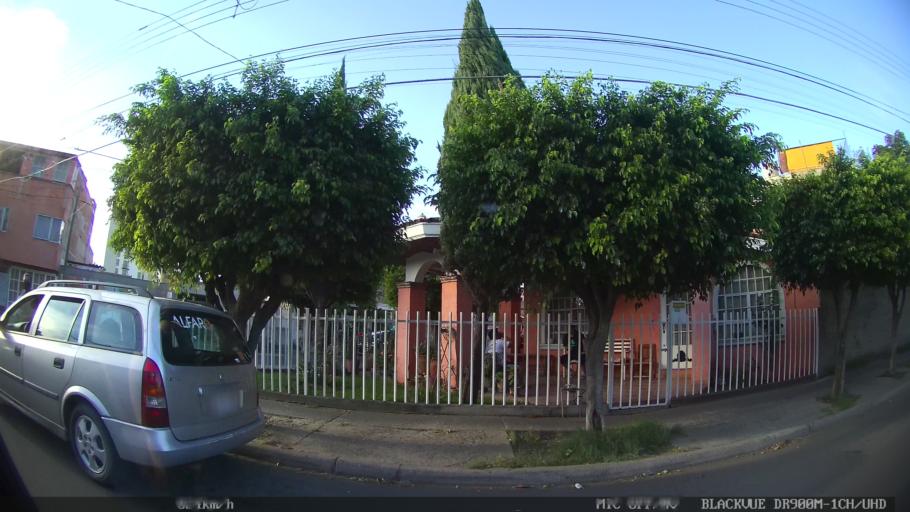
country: MX
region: Jalisco
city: Tlaquepaque
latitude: 20.7103
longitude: -103.3029
